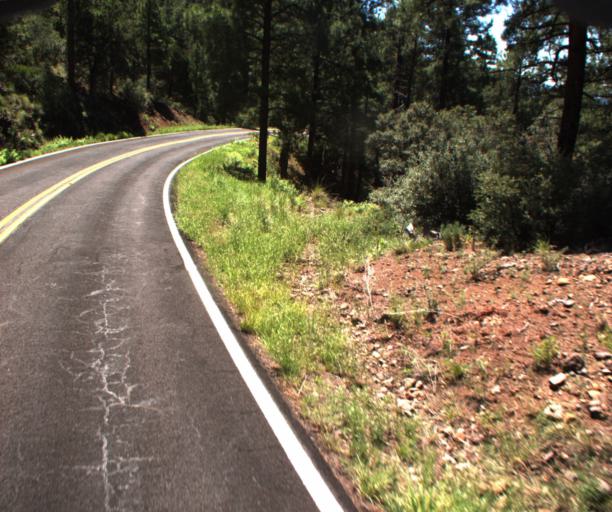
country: US
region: Arizona
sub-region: Greenlee County
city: Morenci
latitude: 33.4297
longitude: -109.3705
